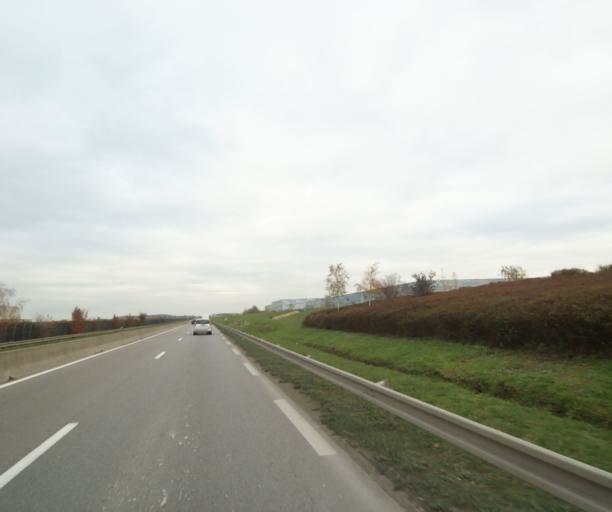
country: FR
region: Ile-de-France
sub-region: Departement du Val-d'Oise
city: Gonesse
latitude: 48.9672
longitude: 2.4549
